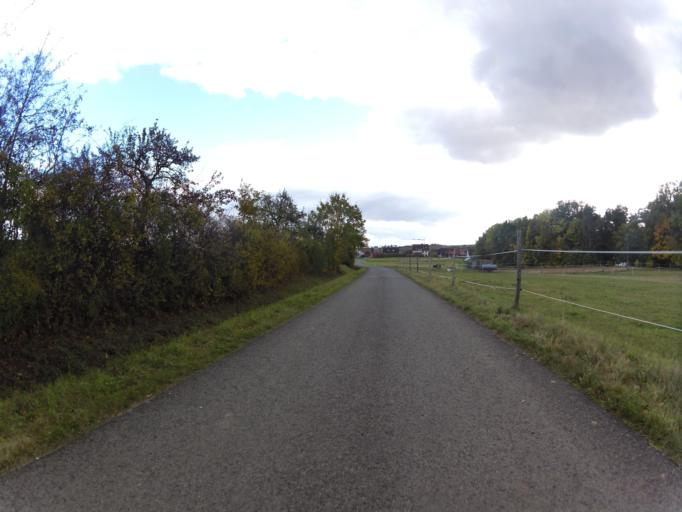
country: DE
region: Bavaria
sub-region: Regierungsbezirk Unterfranken
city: Kurnach
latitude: 49.8626
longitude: 10.0068
